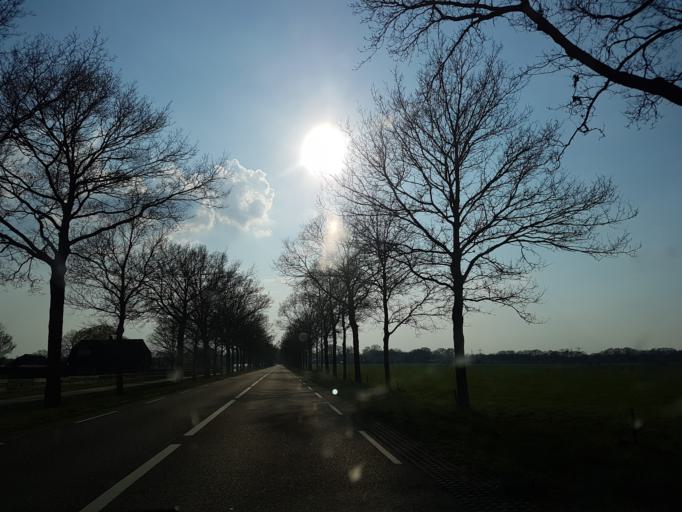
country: NL
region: Overijssel
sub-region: Gemeente Raalte
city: Heino
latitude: 52.4914
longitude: 6.1826
